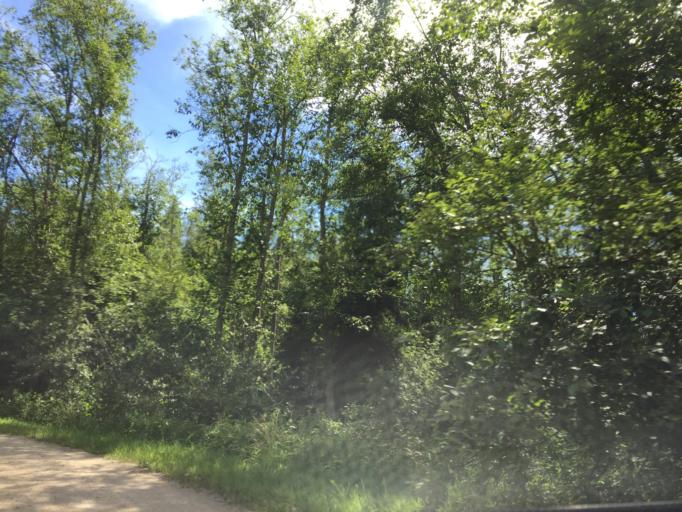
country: LV
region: Kuldigas Rajons
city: Kuldiga
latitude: 57.1153
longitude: 21.8738
